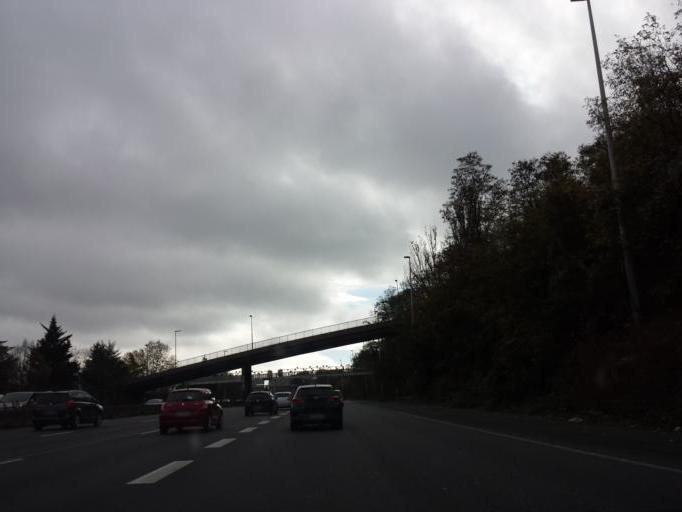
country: FR
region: Ile-de-France
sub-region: Departement du Val-d'Oise
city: Sannois
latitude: 48.9717
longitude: 2.2482
